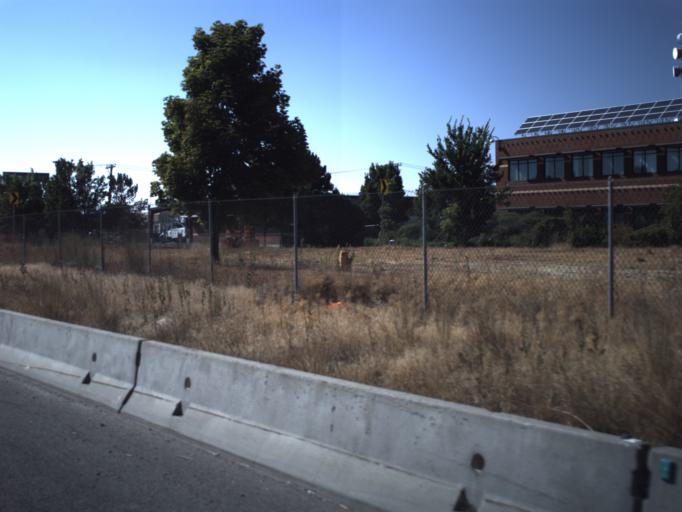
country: US
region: Utah
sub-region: Salt Lake County
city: West Valley City
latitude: 40.7260
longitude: -111.9594
